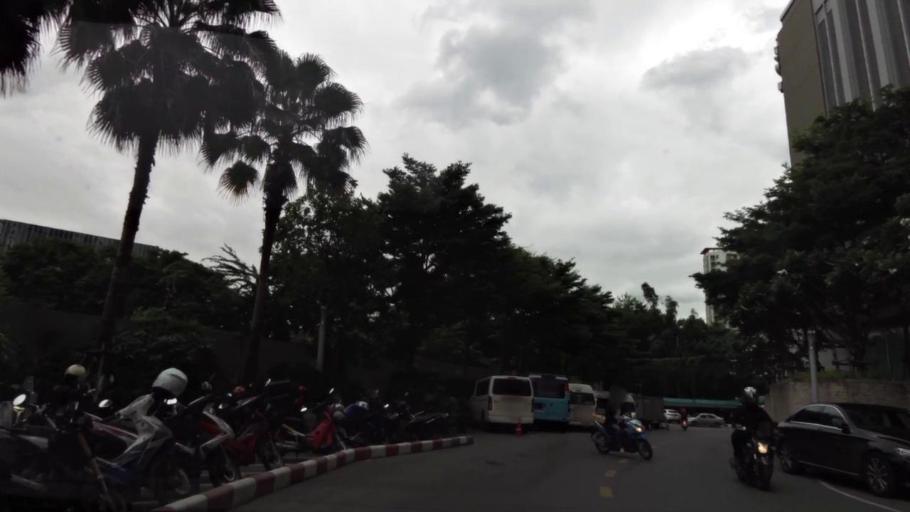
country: TH
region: Bangkok
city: Huai Khwang
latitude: 13.7605
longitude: 100.5697
